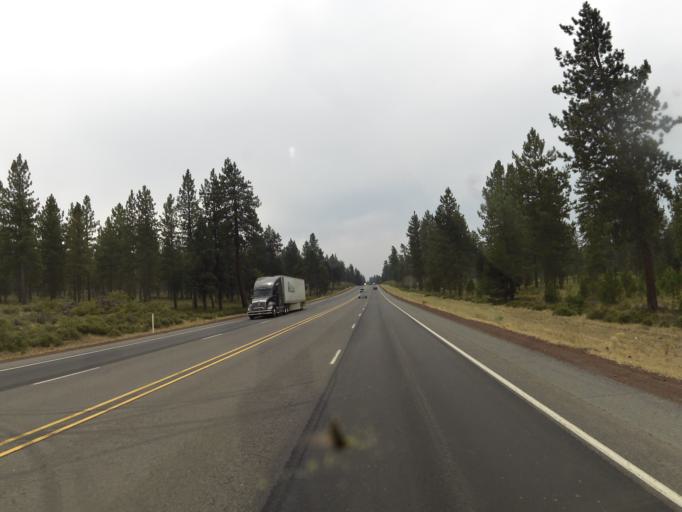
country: US
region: Oregon
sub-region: Deschutes County
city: Three Rivers
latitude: 43.8021
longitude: -121.4388
